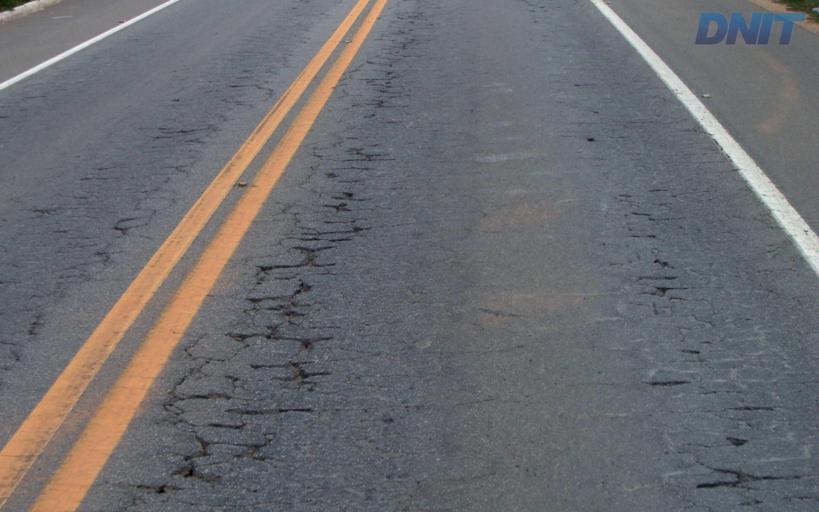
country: BR
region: Minas Gerais
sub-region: Governador Valadares
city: Governador Valadares
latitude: -18.8801
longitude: -41.9941
